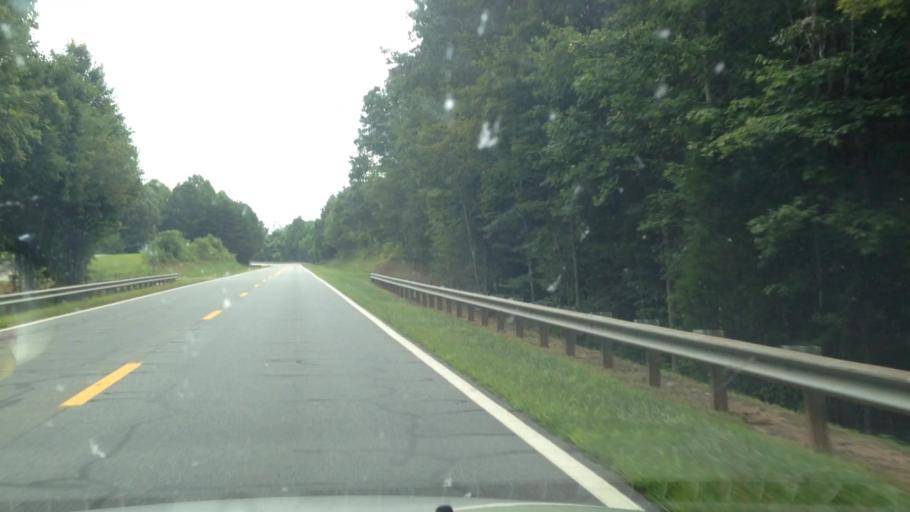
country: US
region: North Carolina
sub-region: Rockingham County
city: Wentworth
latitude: 36.3889
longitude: -79.8151
